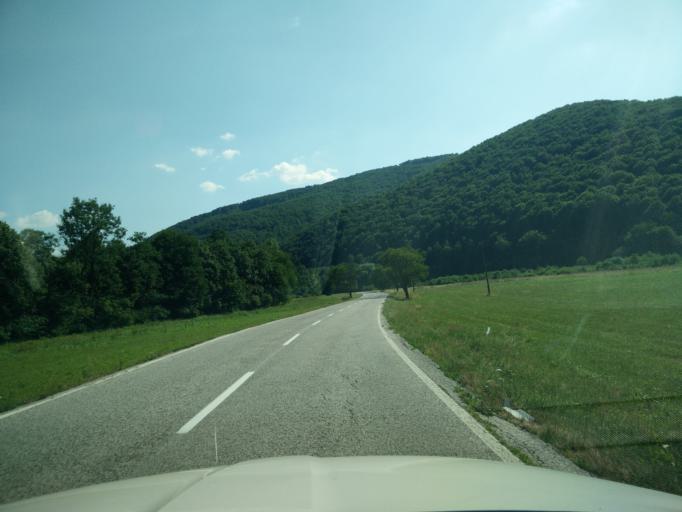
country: SK
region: Nitriansky
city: Bojnice
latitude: 48.8725
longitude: 18.4563
